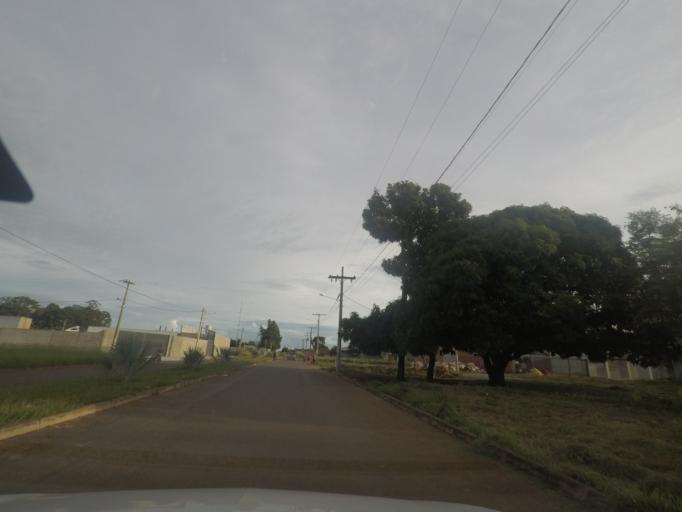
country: BR
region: Goias
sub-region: Trindade
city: Trindade
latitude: -16.7225
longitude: -49.4396
